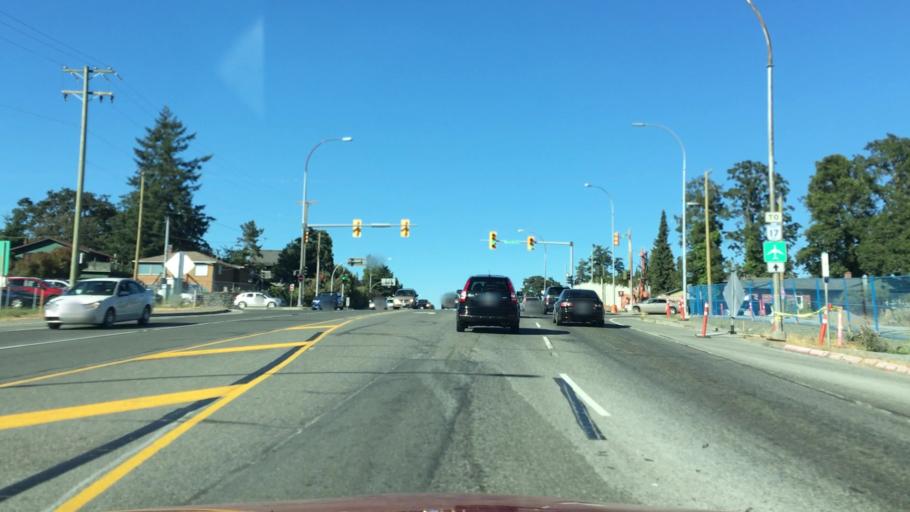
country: CA
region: British Columbia
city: Victoria
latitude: 48.4614
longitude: -123.4028
